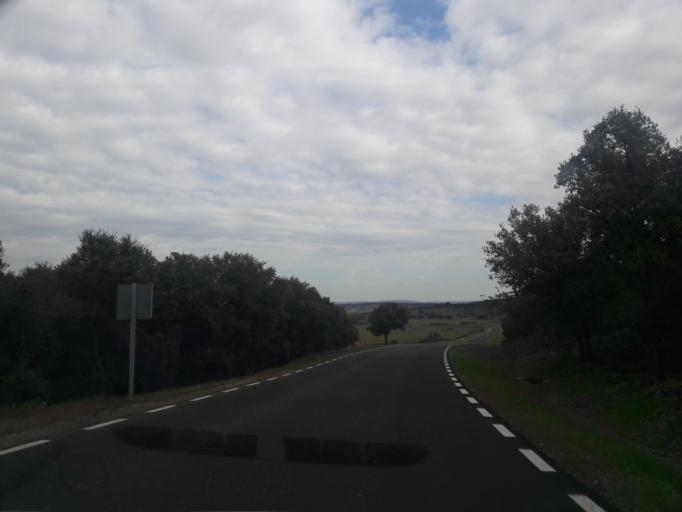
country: ES
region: Castille and Leon
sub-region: Provincia de Salamanca
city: Pastores
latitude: 40.5261
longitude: -6.5252
